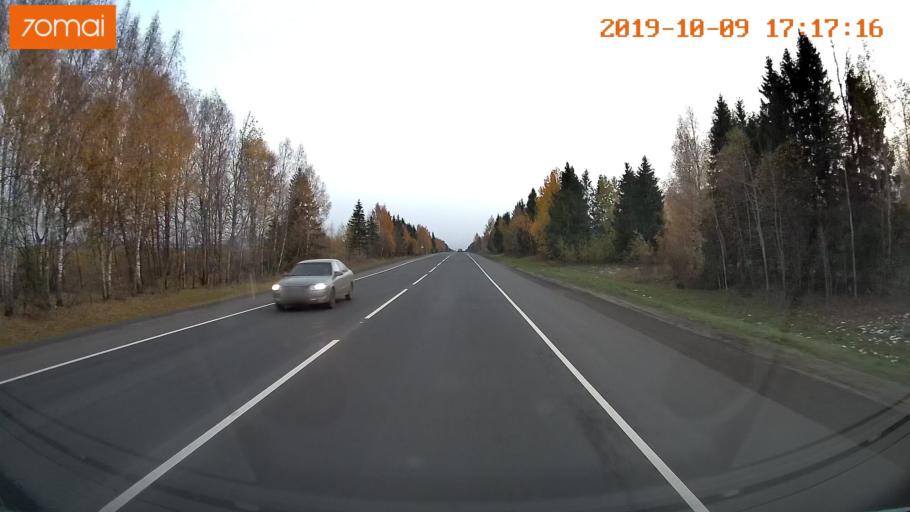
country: RU
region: Ivanovo
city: Furmanov
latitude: 57.2781
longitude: 41.1587
